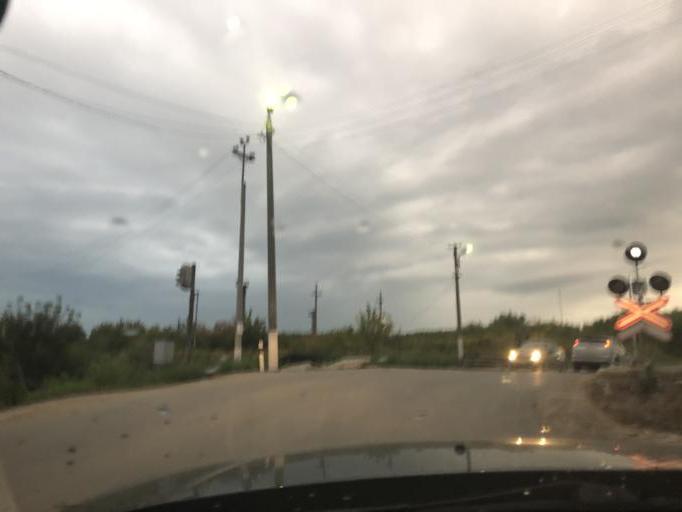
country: RU
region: Tula
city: Gorelki
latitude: 54.2237
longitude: 37.5898
